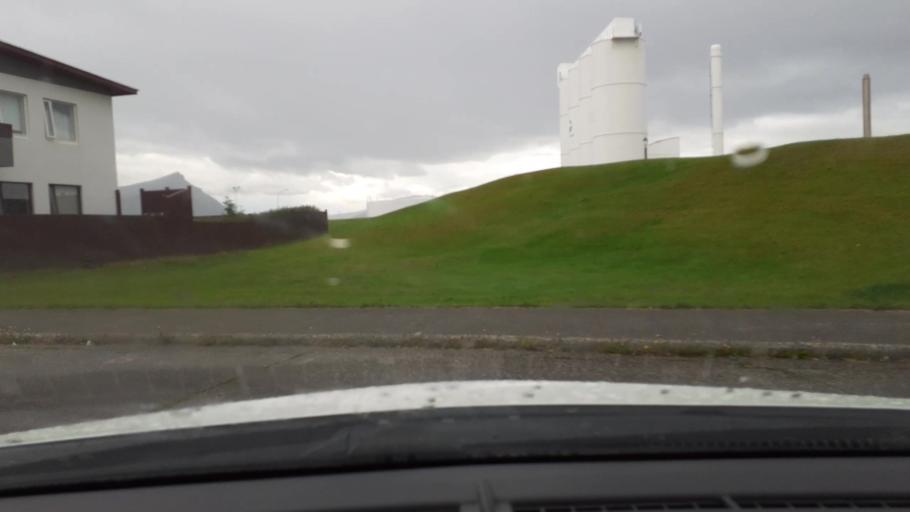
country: IS
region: West
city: Akranes
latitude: 64.3148
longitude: -22.0881
